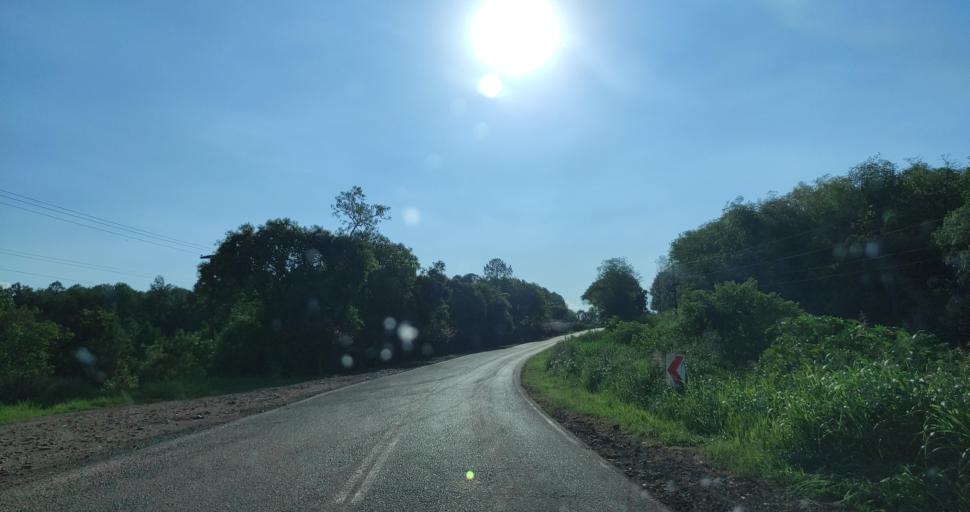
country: AR
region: Misiones
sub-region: Departamento de Eldorado
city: Eldorado
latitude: -26.4059
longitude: -54.4383
